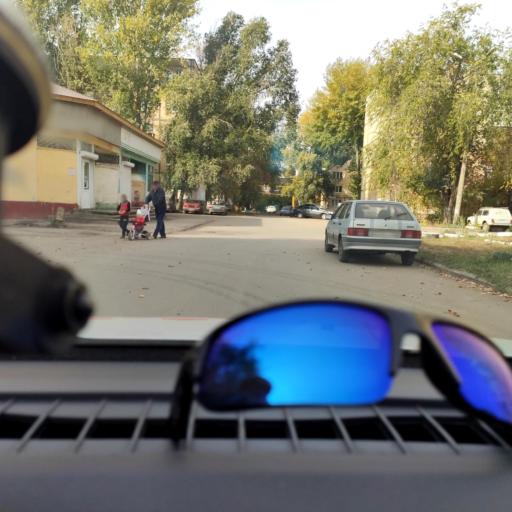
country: RU
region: Samara
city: Samara
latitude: 53.1202
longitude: 50.0921
